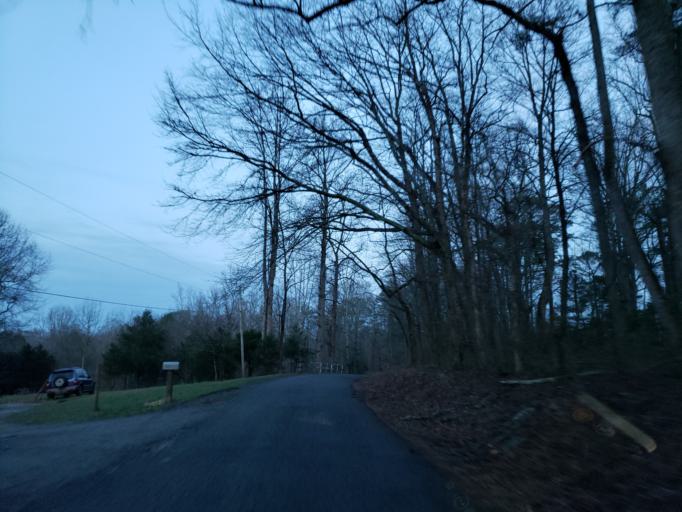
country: US
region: Georgia
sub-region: Cherokee County
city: Ball Ground
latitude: 34.2918
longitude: -84.2918
